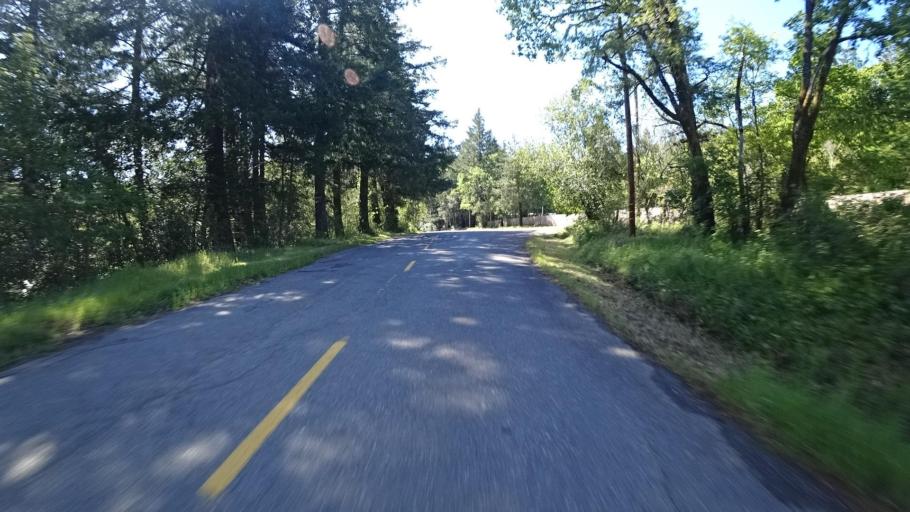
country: US
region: California
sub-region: Humboldt County
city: Rio Dell
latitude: 40.2336
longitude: -124.1547
